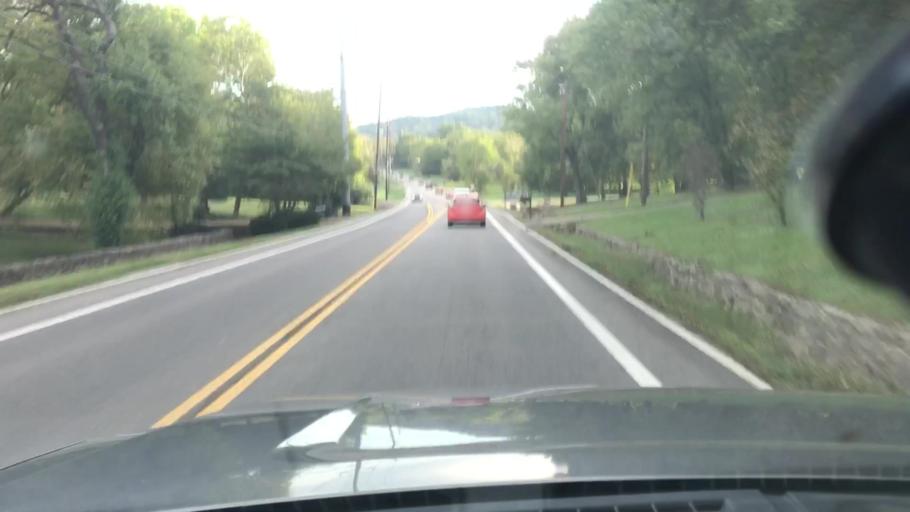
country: US
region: Tennessee
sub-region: Davidson County
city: Forest Hills
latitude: 36.0671
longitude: -86.8450
